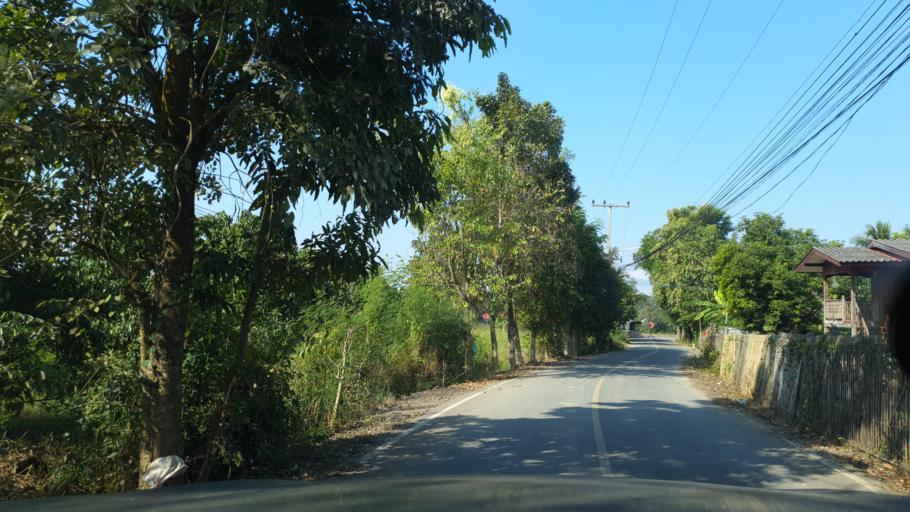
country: TH
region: Chiang Mai
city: Saraphi
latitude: 18.6965
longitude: 99.0851
